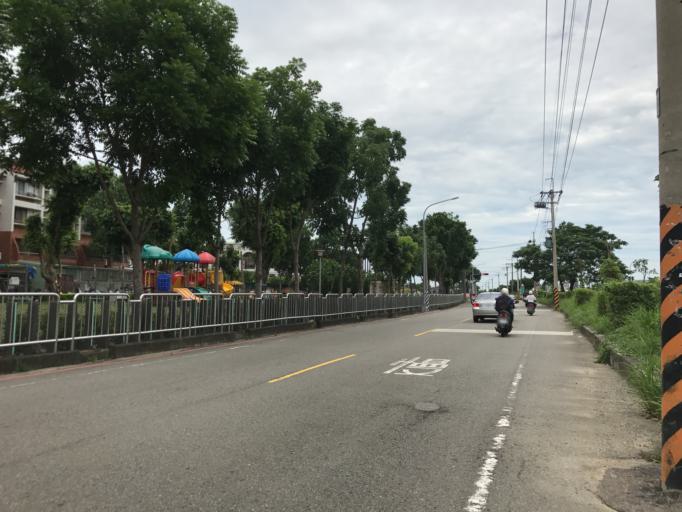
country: TW
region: Taiwan
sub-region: Taichung City
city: Taichung
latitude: 24.0806
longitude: 120.7104
